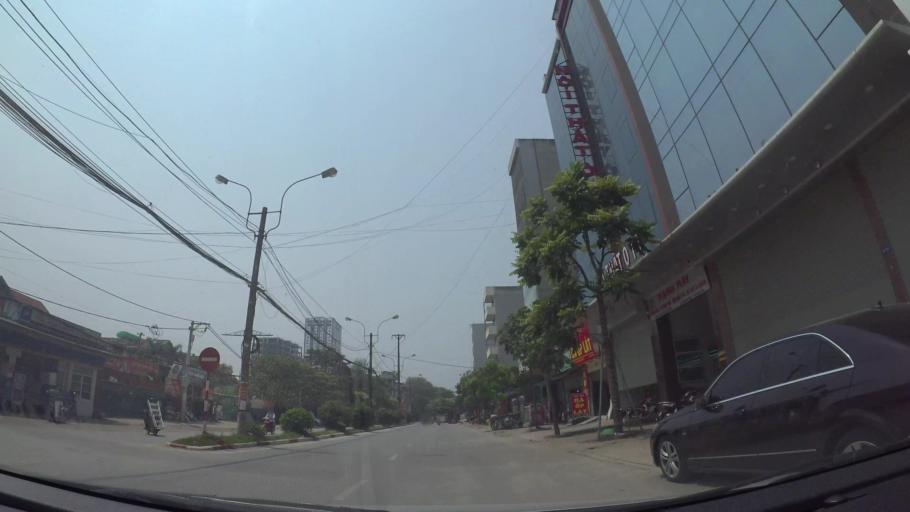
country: VN
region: Ha Noi
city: Ha Dong
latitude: 20.9834
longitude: 105.7699
